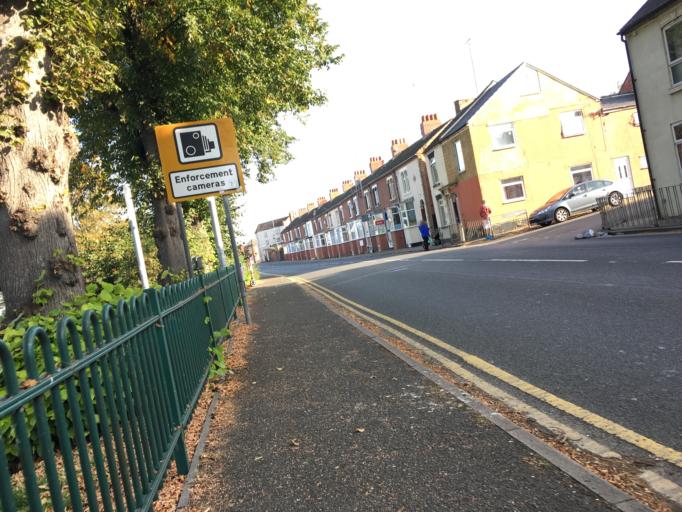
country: GB
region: England
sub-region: Northamptonshire
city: Northampton
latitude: 52.2446
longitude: -0.9041
